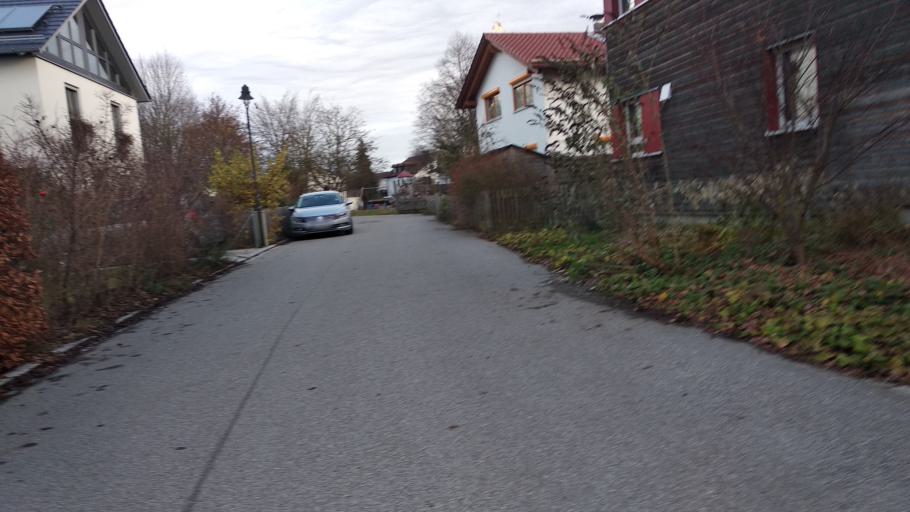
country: DE
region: Bavaria
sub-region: Upper Bavaria
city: Ebersberg
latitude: 48.0806
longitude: 11.9572
